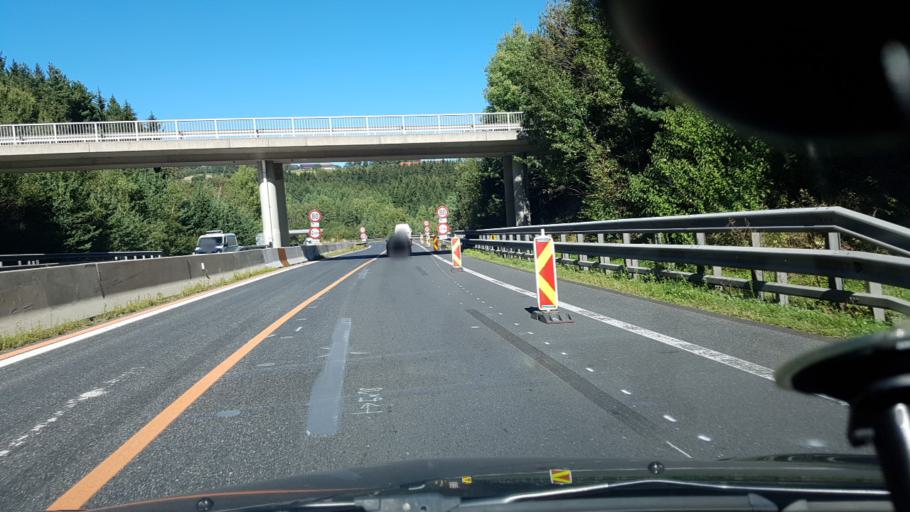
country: AT
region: Lower Austria
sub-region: Politischer Bezirk Neunkirchen
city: Thomasberg
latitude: 47.5524
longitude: 16.1299
